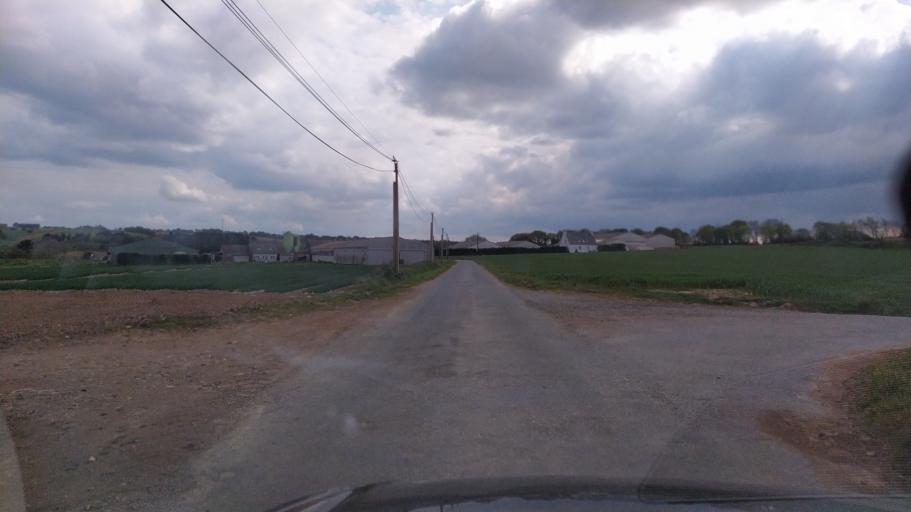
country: FR
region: Brittany
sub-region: Departement du Finistere
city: Bodilis
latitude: 48.5046
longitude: -4.1033
